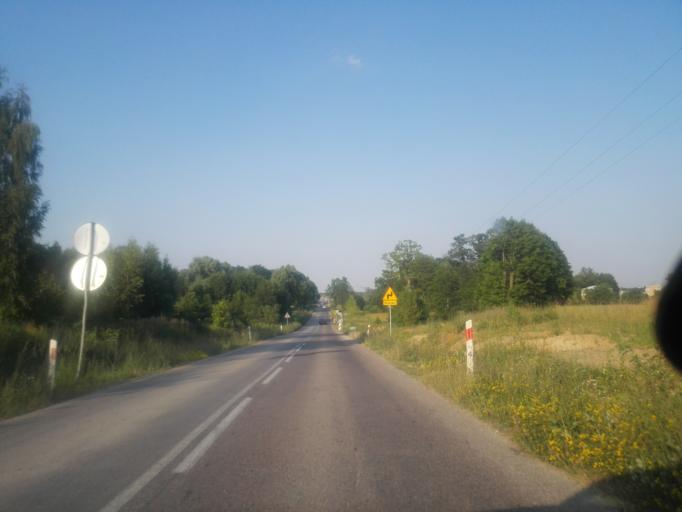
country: PL
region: Podlasie
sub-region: Suwalki
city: Suwalki
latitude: 54.0756
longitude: 23.0470
